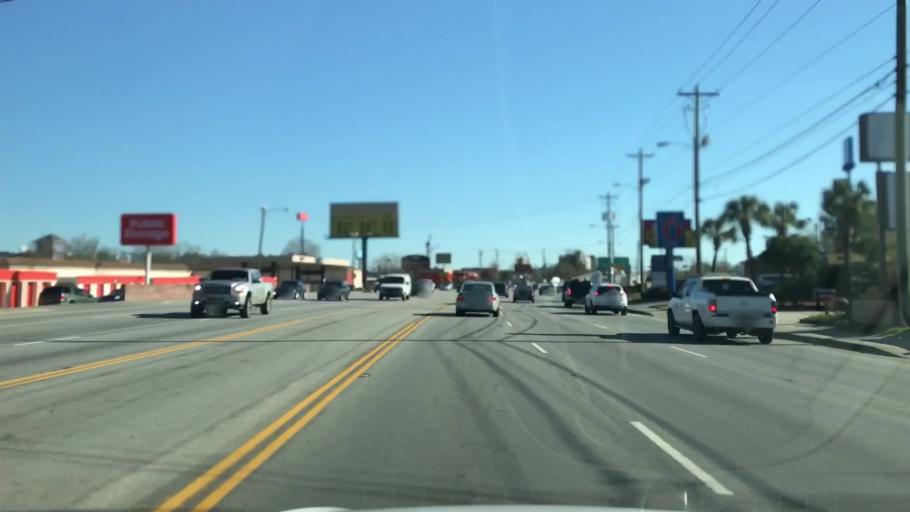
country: US
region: South Carolina
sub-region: Berkeley County
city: Hanahan
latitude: 32.9334
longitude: -80.0529
